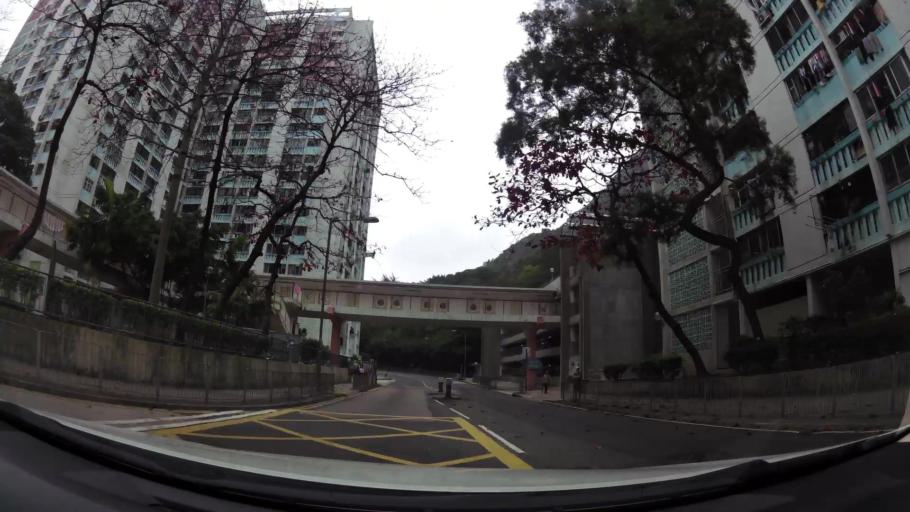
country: HK
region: Kowloon City
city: Kowloon
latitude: 22.3326
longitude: 114.2248
